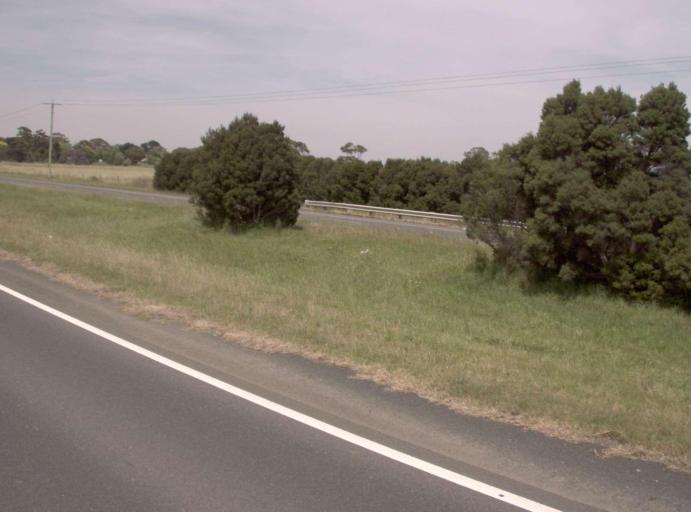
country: AU
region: Victoria
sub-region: Casey
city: Lynbrook
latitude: -38.0720
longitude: 145.2408
